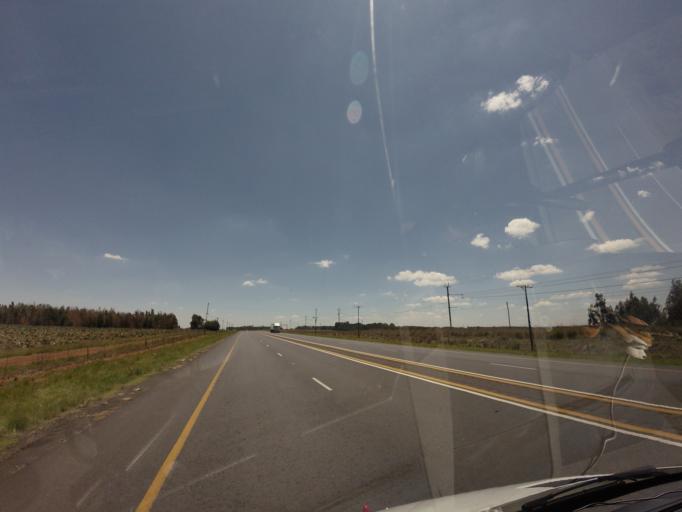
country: ZA
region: Mpumalanga
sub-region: Nkangala District Municipality
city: Belfast
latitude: -25.7280
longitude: 30.0271
